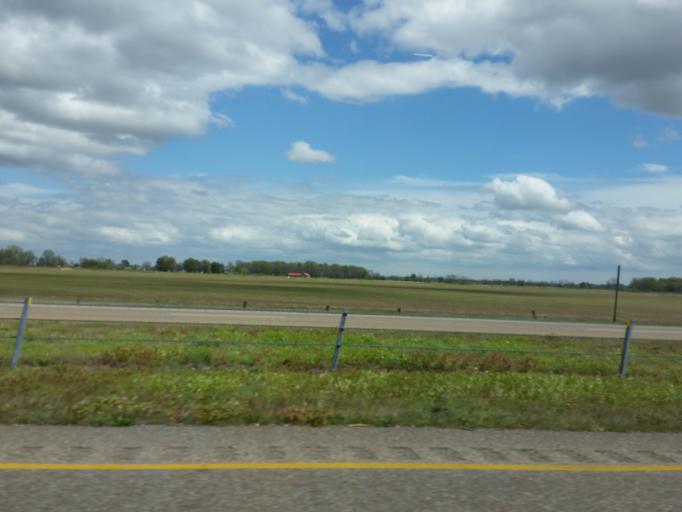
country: US
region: Arkansas
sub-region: Crittenden County
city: Marion
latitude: 35.2789
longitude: -90.2367
